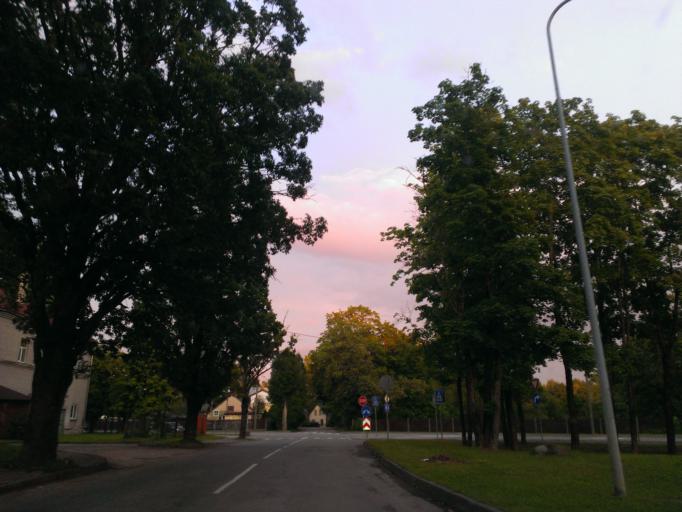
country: LV
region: Ogre
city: Ogre
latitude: 56.8129
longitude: 24.6011
